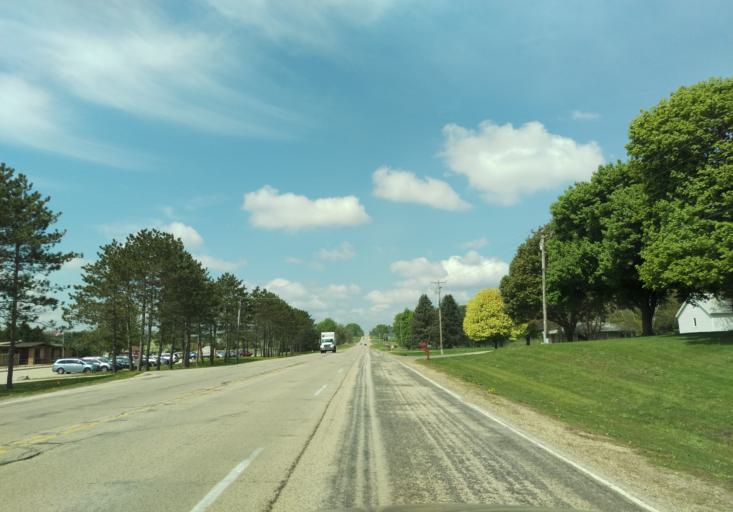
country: US
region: Wisconsin
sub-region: Dane County
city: Middleton
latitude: 43.0603
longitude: -89.5777
